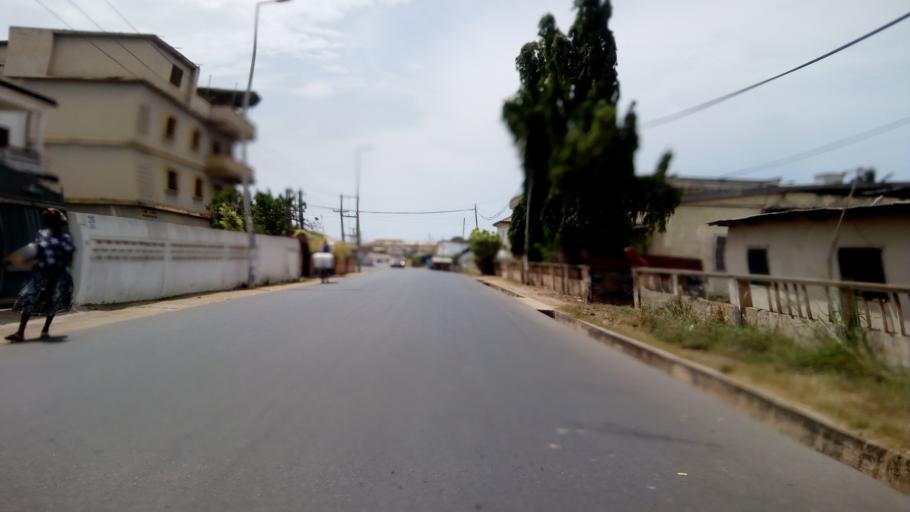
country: GH
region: Central
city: Cape Coast
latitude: 5.1282
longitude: -1.2749
